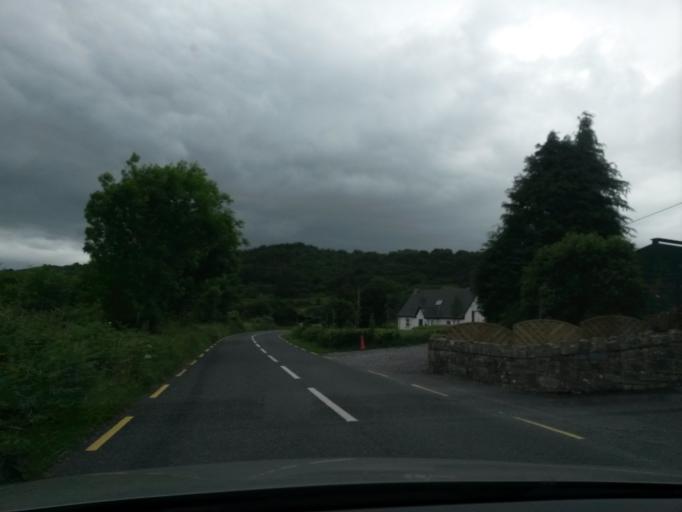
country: IE
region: Connaught
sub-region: Sligo
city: Sligo
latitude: 54.2628
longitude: -8.3220
